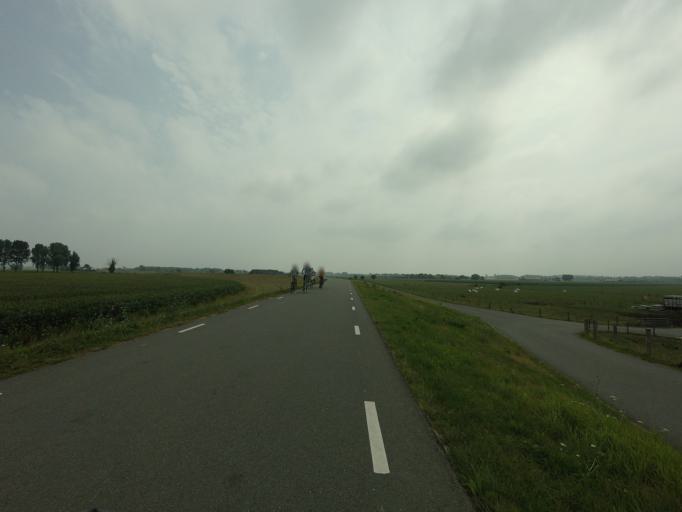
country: NL
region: Utrecht
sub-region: Gemeente Wijk bij Duurstede
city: Wijk bij Duurstede
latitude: 51.9620
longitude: 5.3699
